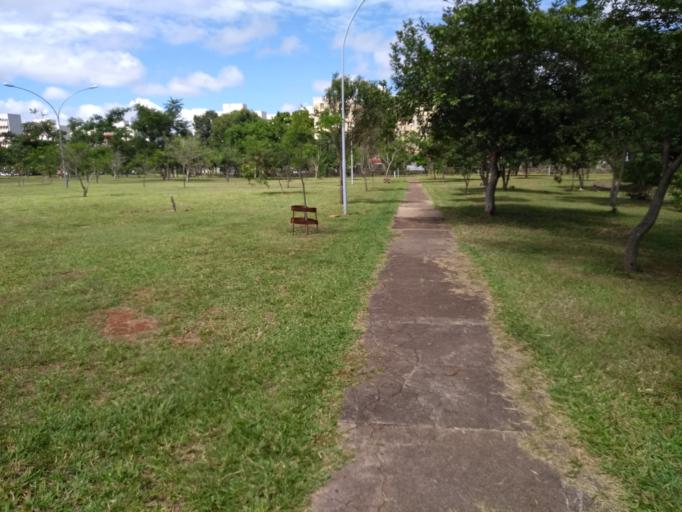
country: BR
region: Federal District
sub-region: Brasilia
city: Brasilia
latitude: -15.8054
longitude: -47.9434
